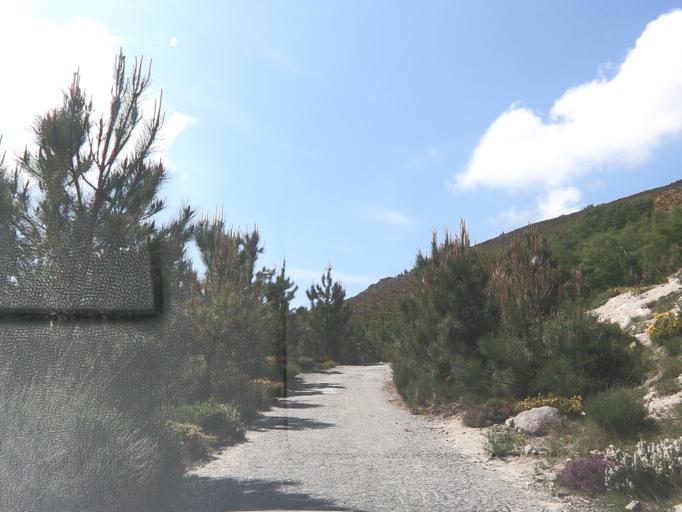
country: PT
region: Vila Real
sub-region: Vila Real
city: Vila Real
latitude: 41.3691
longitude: -7.7467
